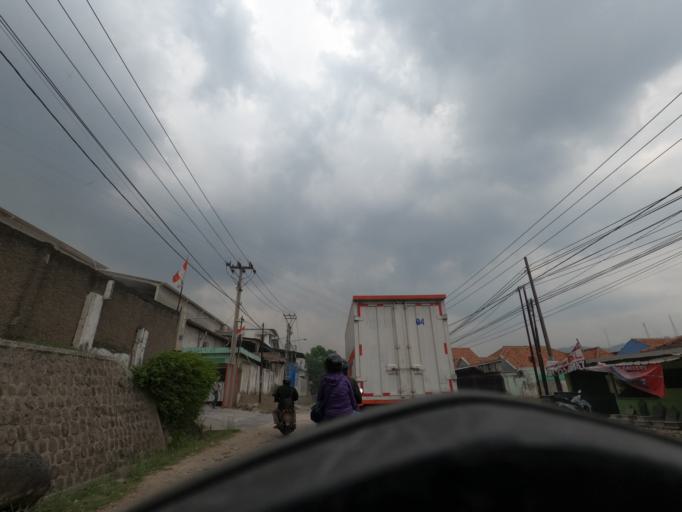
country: ID
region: West Java
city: Padalarang
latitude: -6.8323
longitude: 107.4611
